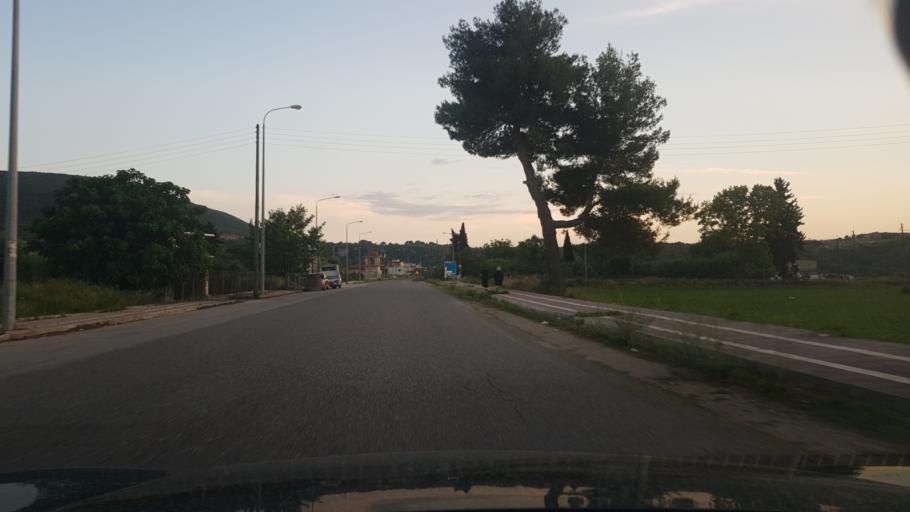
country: GR
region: West Greece
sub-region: Nomos Aitolias kai Akarnanias
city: Vonitsa
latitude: 38.9113
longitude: 20.8880
